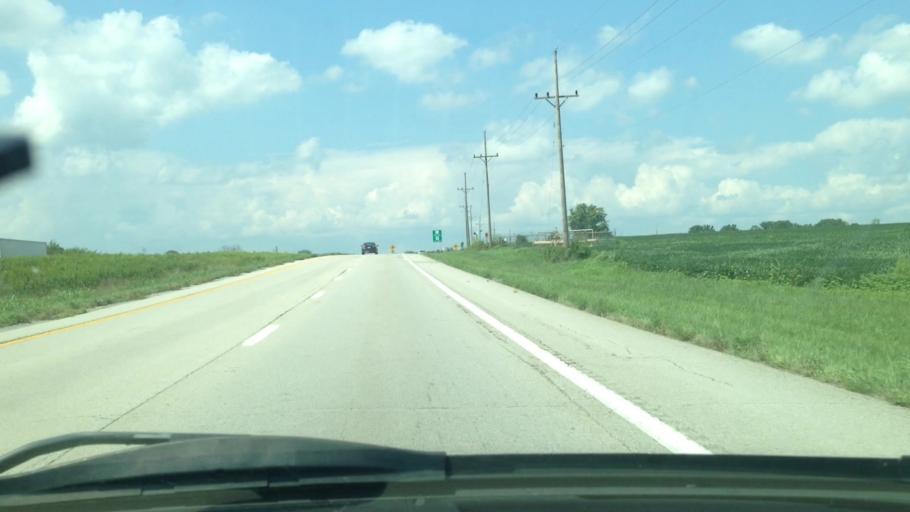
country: US
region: Missouri
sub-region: Lincoln County
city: Troy
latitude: 39.1221
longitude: -90.9621
